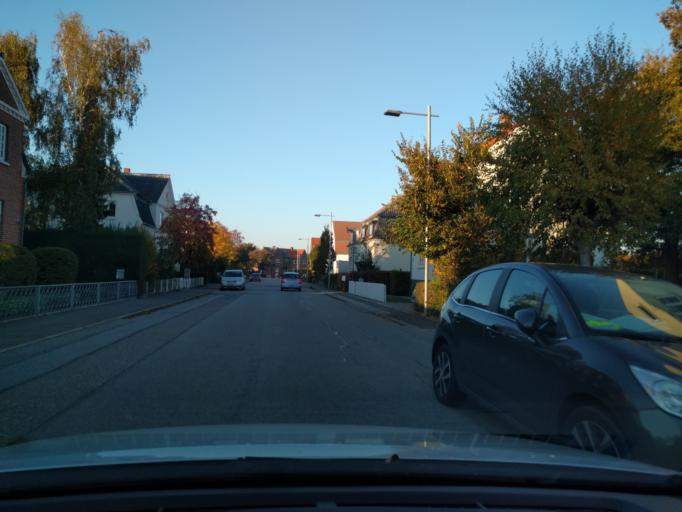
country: DK
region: Zealand
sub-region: Guldborgsund Kommune
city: Nykobing Falster
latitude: 54.7639
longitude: 11.8859
